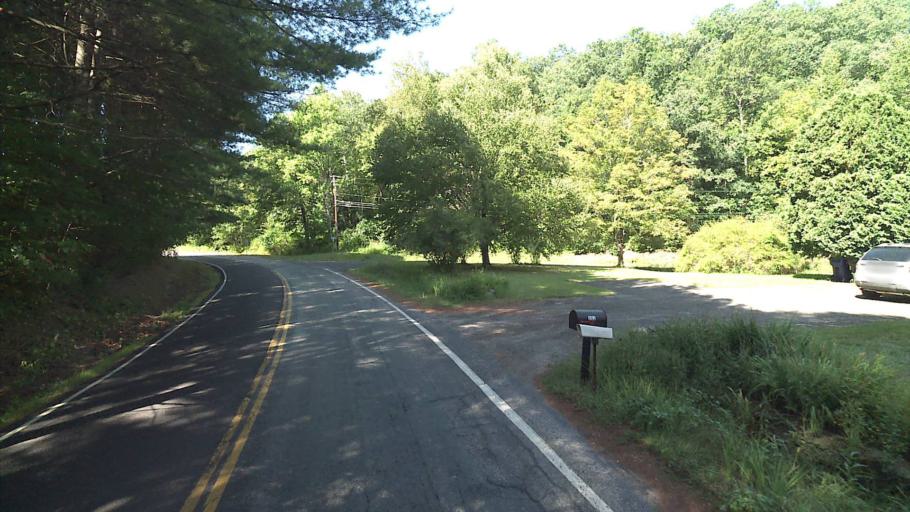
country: US
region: Connecticut
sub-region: Litchfield County
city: Thomaston
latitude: 41.7096
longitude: -73.0604
